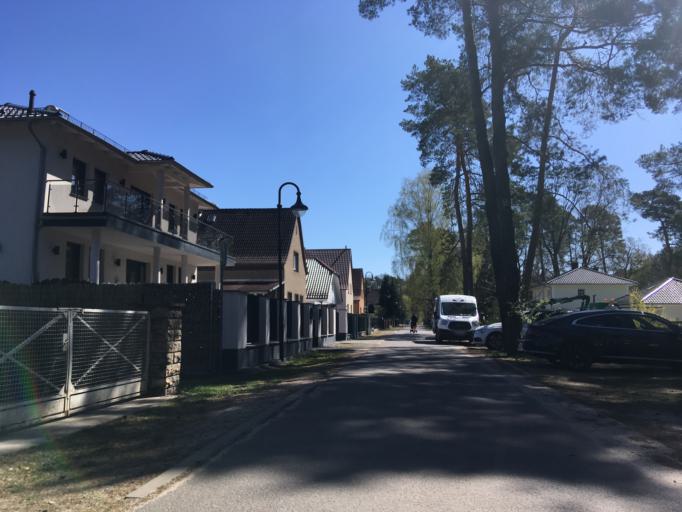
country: DE
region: Brandenburg
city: Bernau bei Berlin
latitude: 52.6970
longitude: 13.5448
